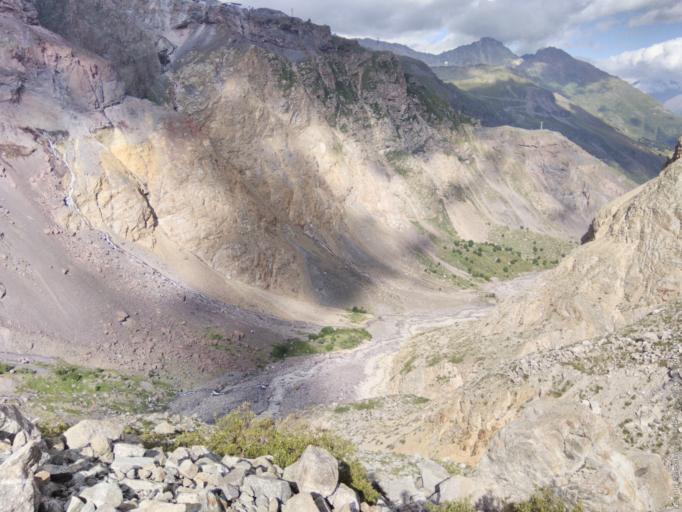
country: RU
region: Kabardino-Balkariya
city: Terskol
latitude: 43.2676
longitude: 42.4474
